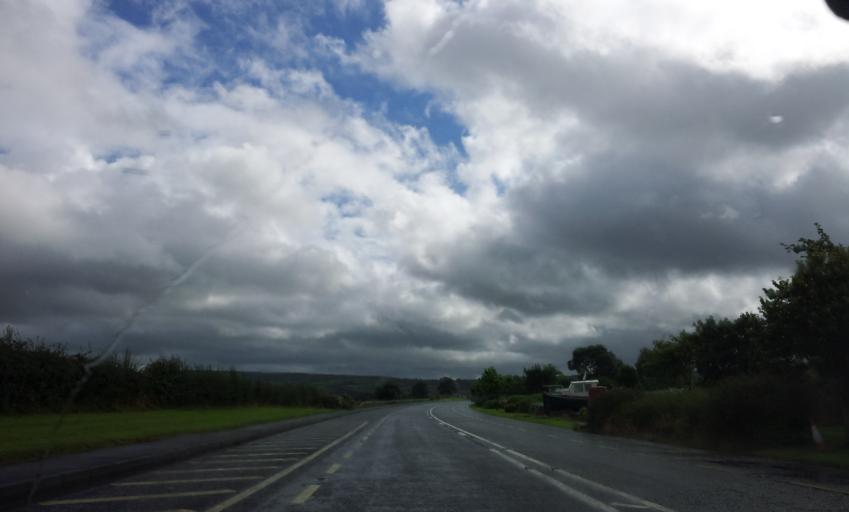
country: IE
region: Munster
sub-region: Waterford
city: Dungarvan
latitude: 52.0793
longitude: -7.6361
